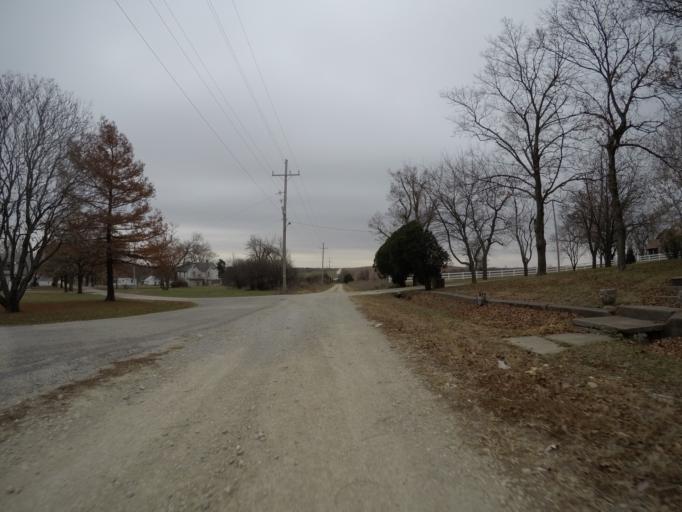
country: US
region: Kansas
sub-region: Wabaunsee County
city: Alma
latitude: 38.8577
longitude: -96.1134
